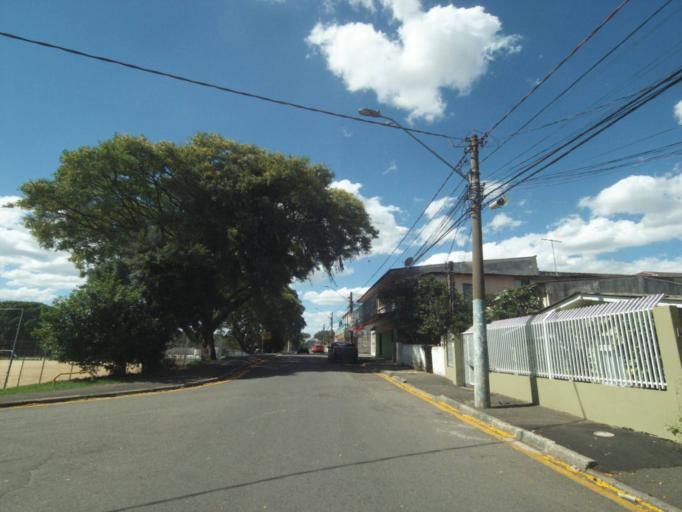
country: BR
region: Parana
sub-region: Curitiba
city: Curitiba
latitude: -25.5065
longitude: -49.3239
